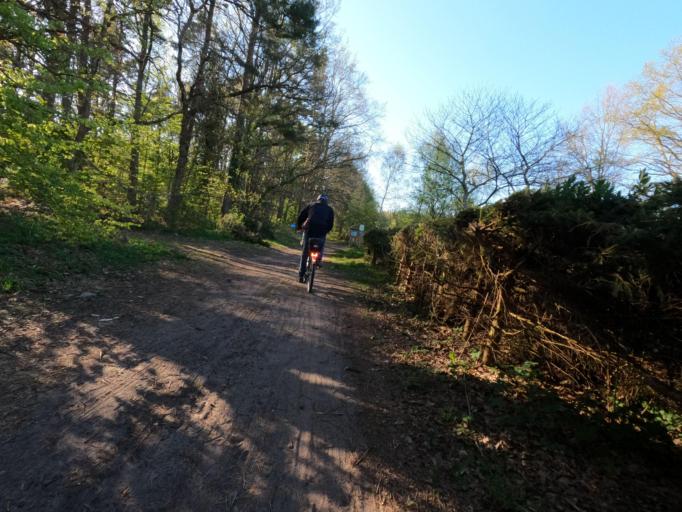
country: DE
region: Mecklenburg-Vorpommern
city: Born
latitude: 54.3931
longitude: 12.5355
